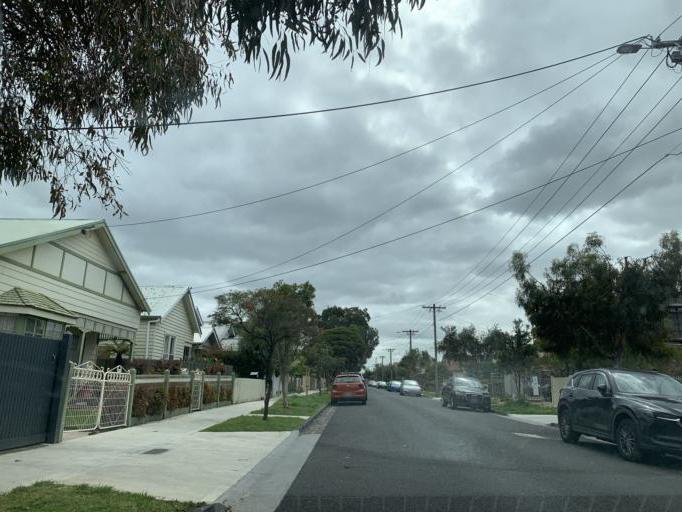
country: AU
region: Victoria
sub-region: Moreland
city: Pascoe Vale South
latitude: -37.7520
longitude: 144.9498
